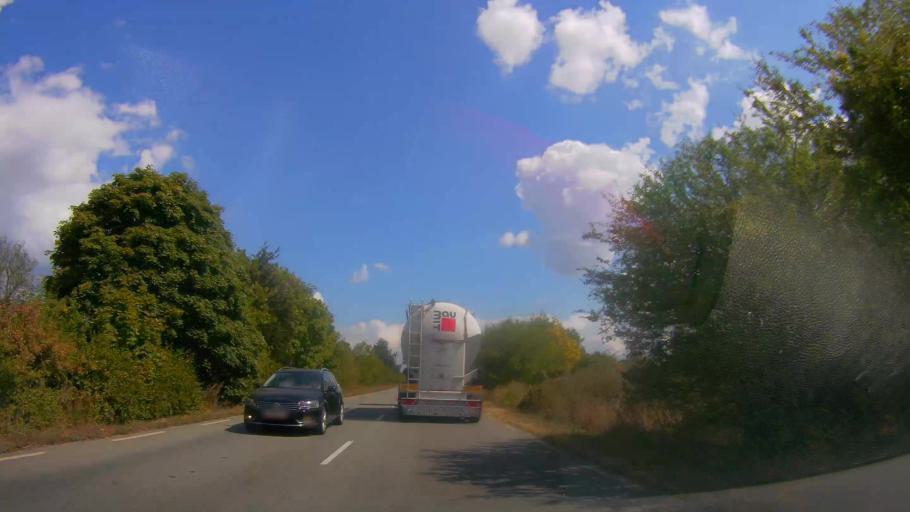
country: BG
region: Sliven
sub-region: Obshtina Tvurditsa
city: Tvurditsa
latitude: 42.6566
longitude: 25.9283
